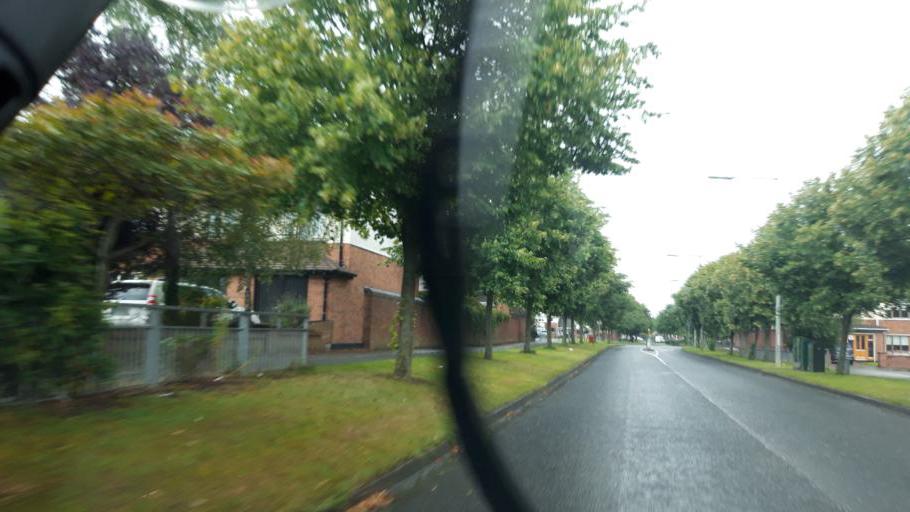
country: IE
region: Leinster
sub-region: Fingal County
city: Blanchardstown
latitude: 53.3715
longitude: -6.3965
